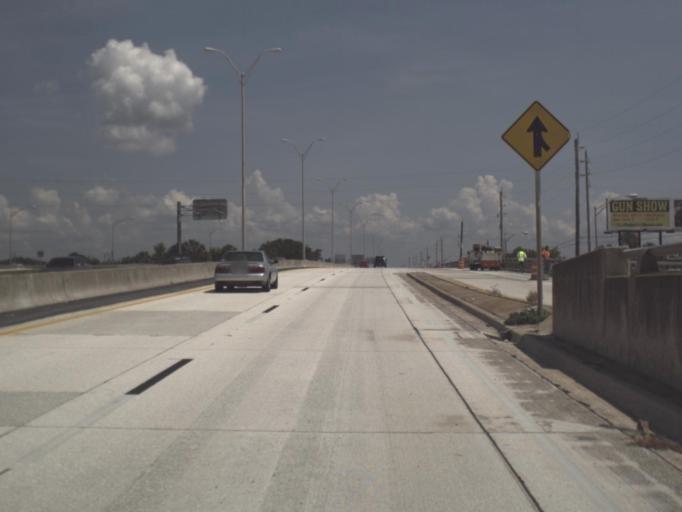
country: US
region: Florida
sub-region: Duval County
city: Jacksonville
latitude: 30.3320
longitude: -81.6366
